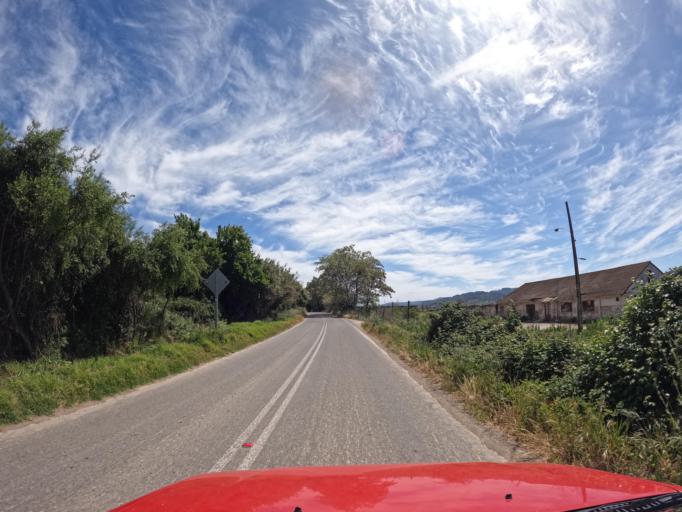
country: CL
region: Maule
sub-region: Provincia de Talca
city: Talca
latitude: -34.9887
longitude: -71.8288
